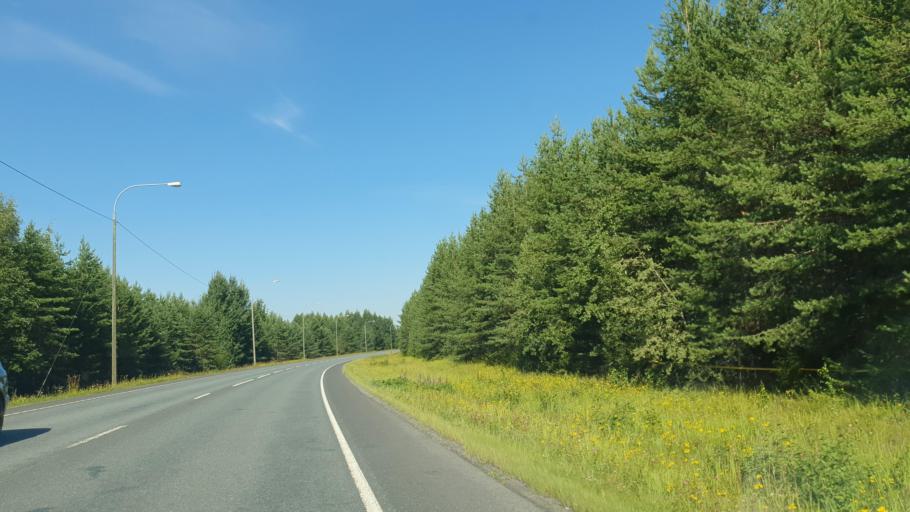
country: FI
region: Northern Savo
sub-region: Kuopio
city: Siilinjaervi
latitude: 63.1632
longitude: 27.5684
